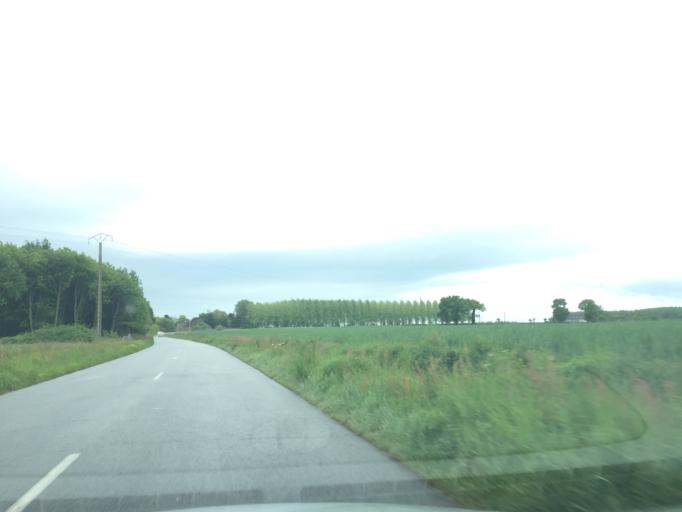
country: FR
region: Brittany
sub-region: Departement des Cotes-d'Armor
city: Crehen
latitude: 48.5578
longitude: -2.2402
